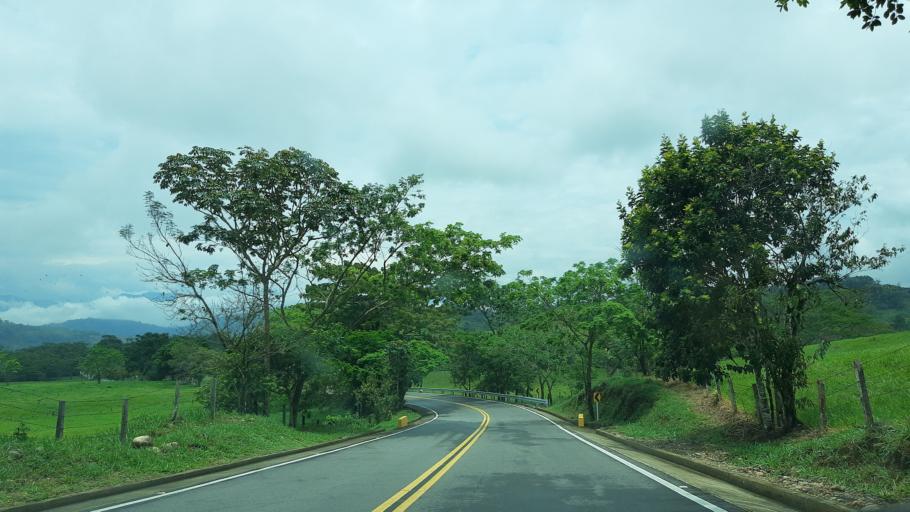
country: CO
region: Casanare
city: Sabanalarga
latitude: 4.7937
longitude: -73.0542
